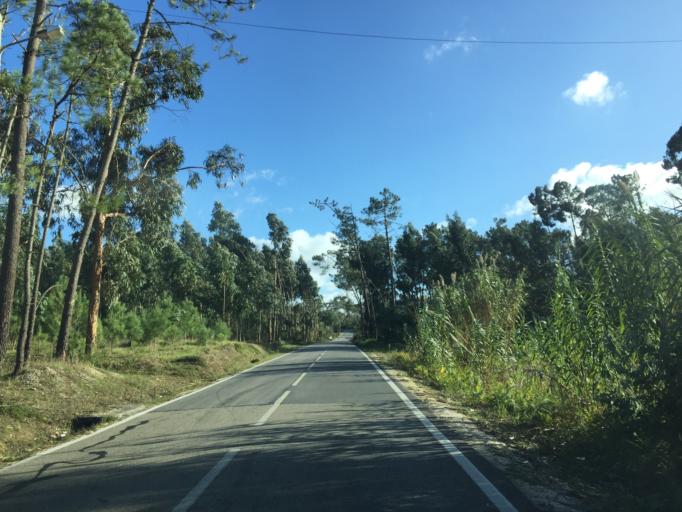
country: PT
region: Coimbra
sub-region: Figueira da Foz
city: Tavarede
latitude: 40.2037
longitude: -8.8370
